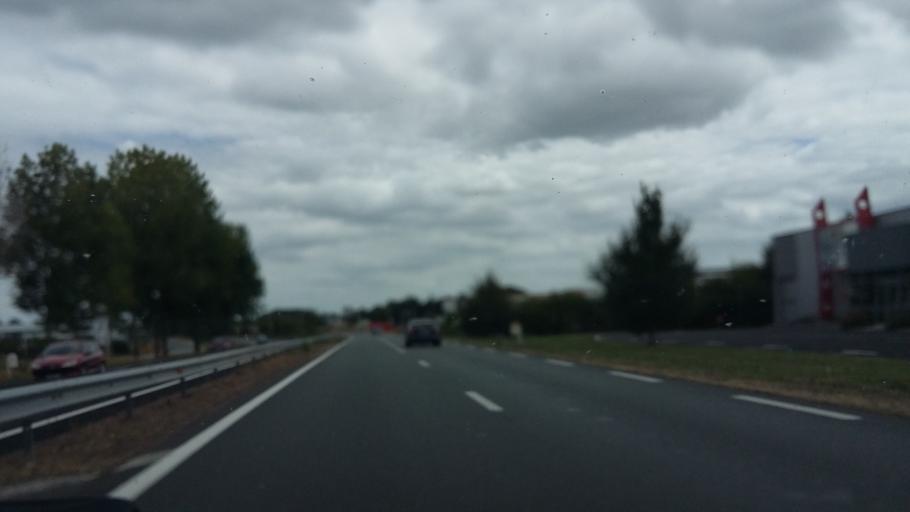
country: FR
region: Pays de la Loire
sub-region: Departement de la Vendee
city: Aizenay
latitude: 46.7256
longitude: -1.5675
